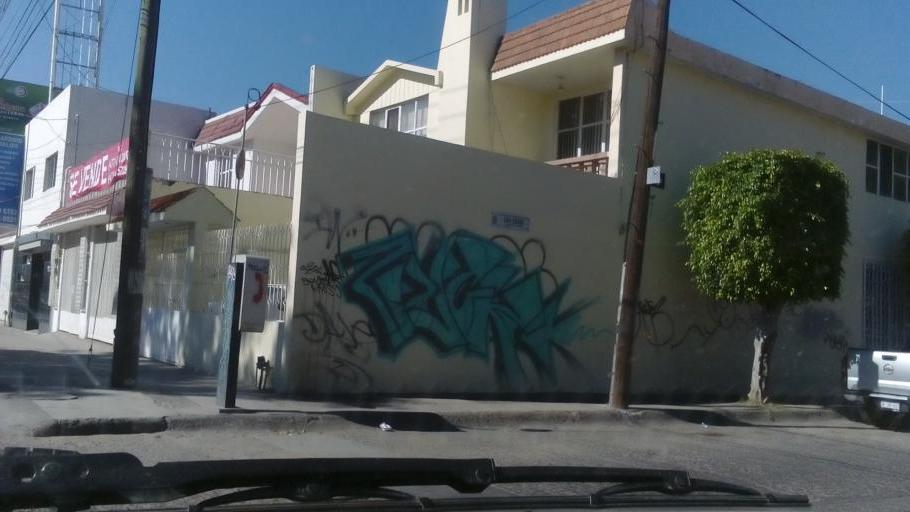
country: MX
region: Guanajuato
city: Leon
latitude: 21.1450
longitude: -101.6731
